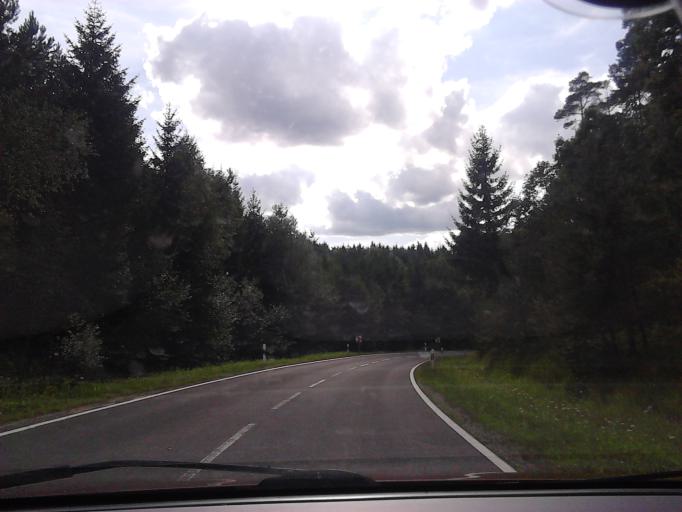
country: DE
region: Bavaria
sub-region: Upper Franconia
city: Weitramsdorf
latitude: 50.2619
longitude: 10.8349
